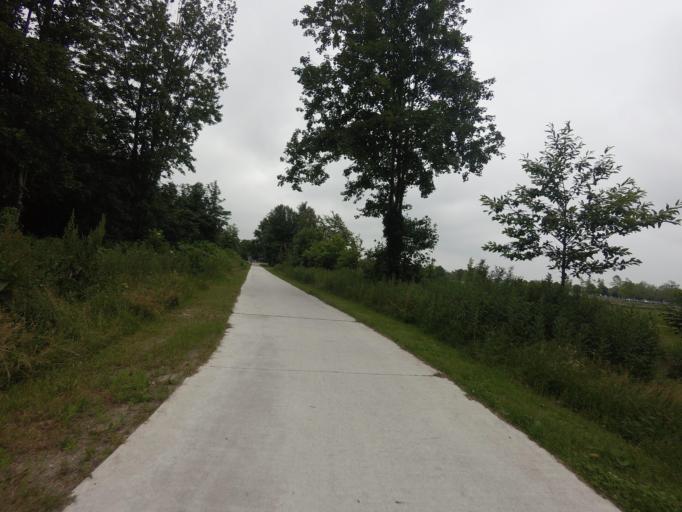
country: NL
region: Flevoland
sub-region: Gemeente Almere
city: Almere Stad
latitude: 52.3967
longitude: 5.2859
